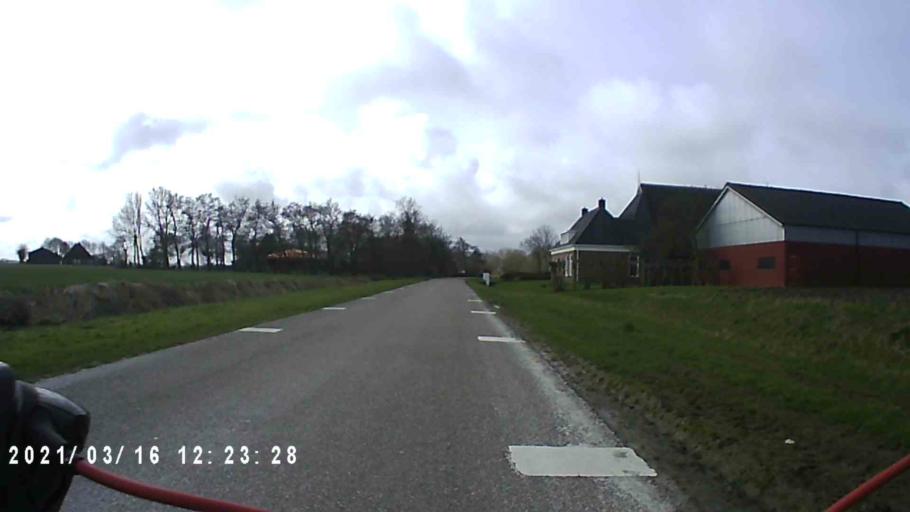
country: NL
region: Friesland
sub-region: Gemeente Ferwerderadiel
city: Hallum
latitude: 53.3026
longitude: 5.7548
